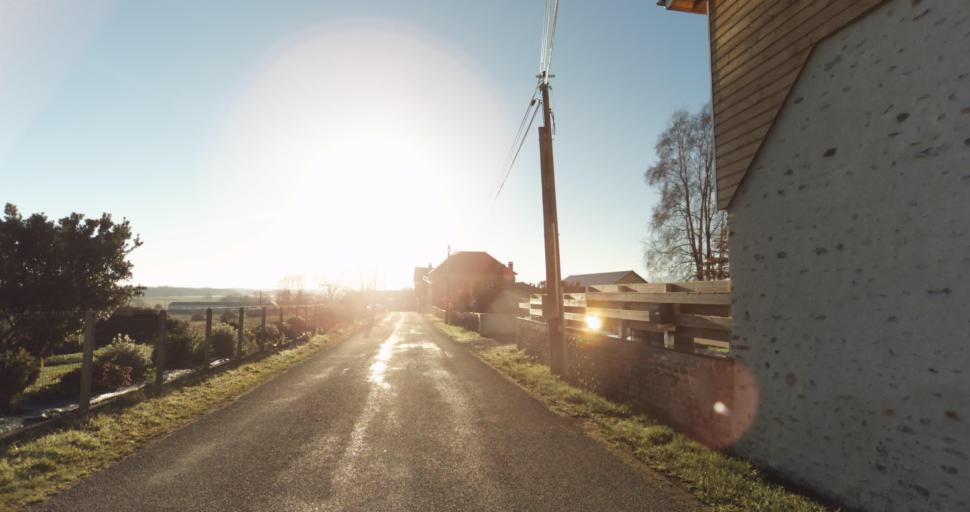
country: FR
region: Aquitaine
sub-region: Departement des Pyrenees-Atlantiques
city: Morlaas
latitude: 43.3242
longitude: -0.2554
